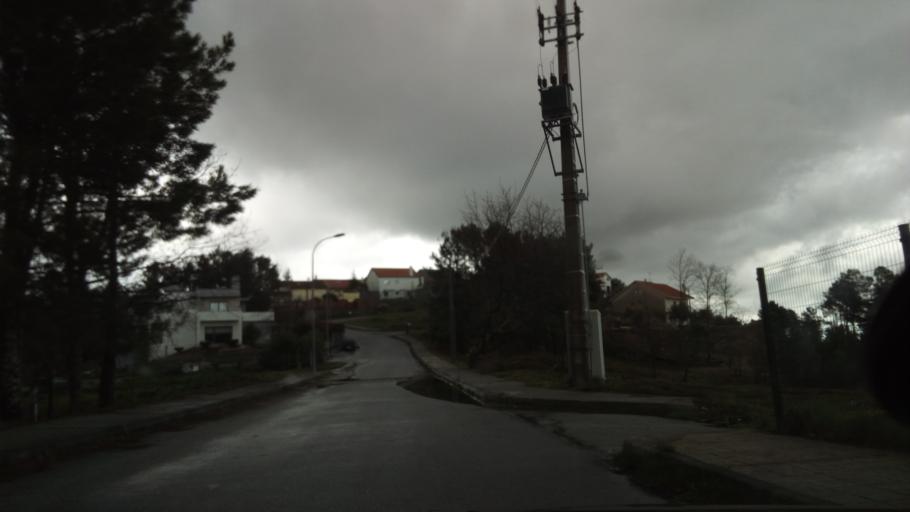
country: PT
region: Guarda
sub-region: Fornos de Algodres
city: Fornos de Algodres
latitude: 40.6260
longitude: -7.5433
